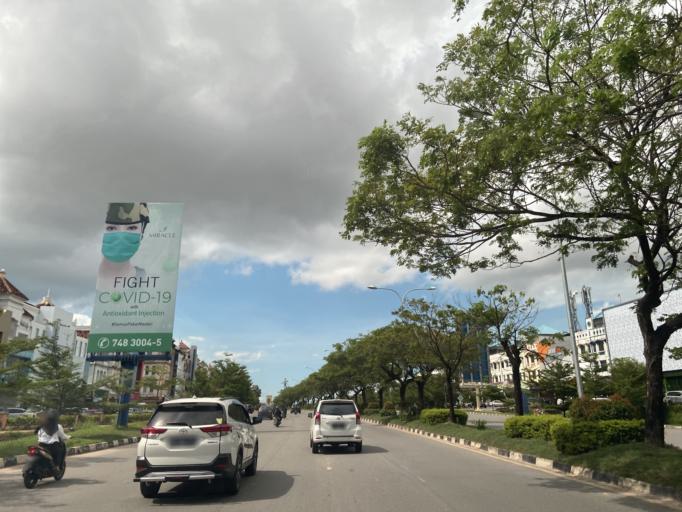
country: SG
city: Singapore
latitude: 1.1293
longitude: 104.0378
